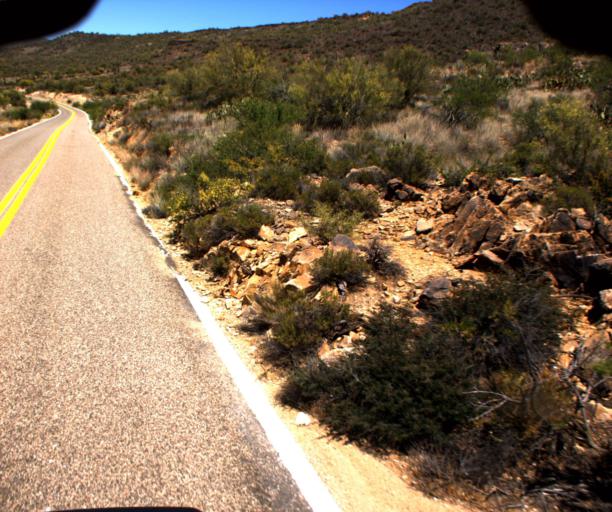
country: US
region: Arizona
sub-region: Yavapai County
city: Bagdad
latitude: 34.5119
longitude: -113.0769
